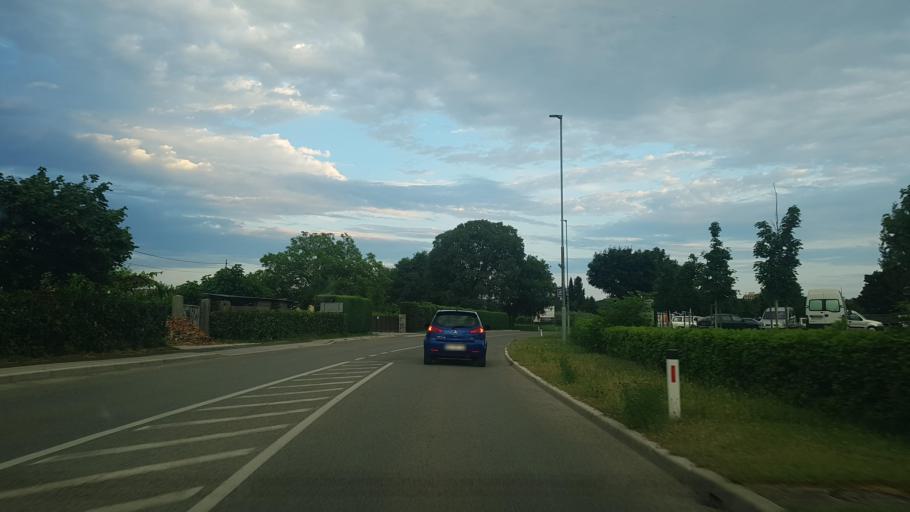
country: SI
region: Nova Gorica
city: Solkan
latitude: 45.9656
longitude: 13.6484
